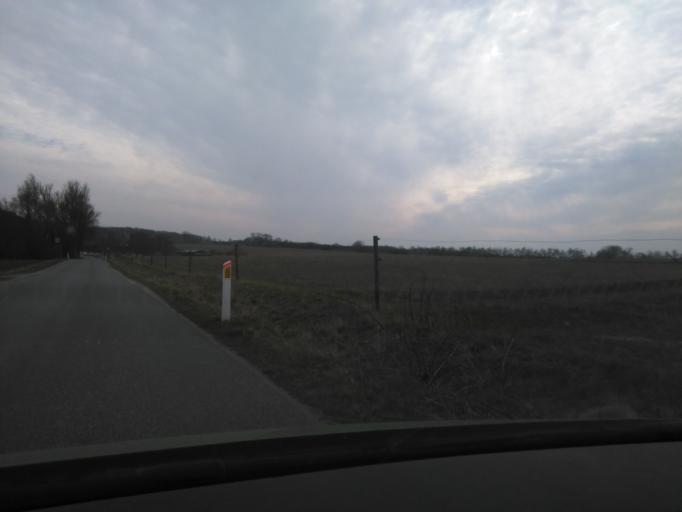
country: DK
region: Central Jutland
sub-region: Arhus Kommune
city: Beder
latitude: 56.0767
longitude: 10.2350
